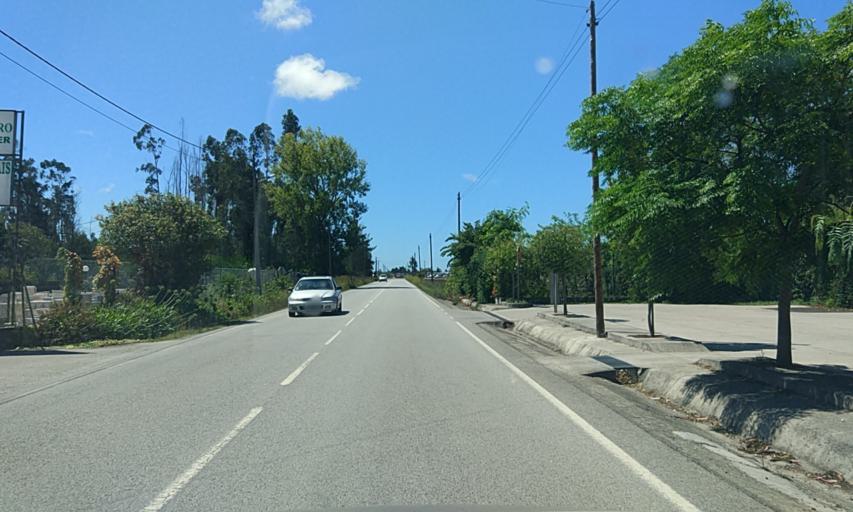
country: PT
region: Coimbra
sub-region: Mira
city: Mira
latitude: 40.4534
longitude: -8.7131
